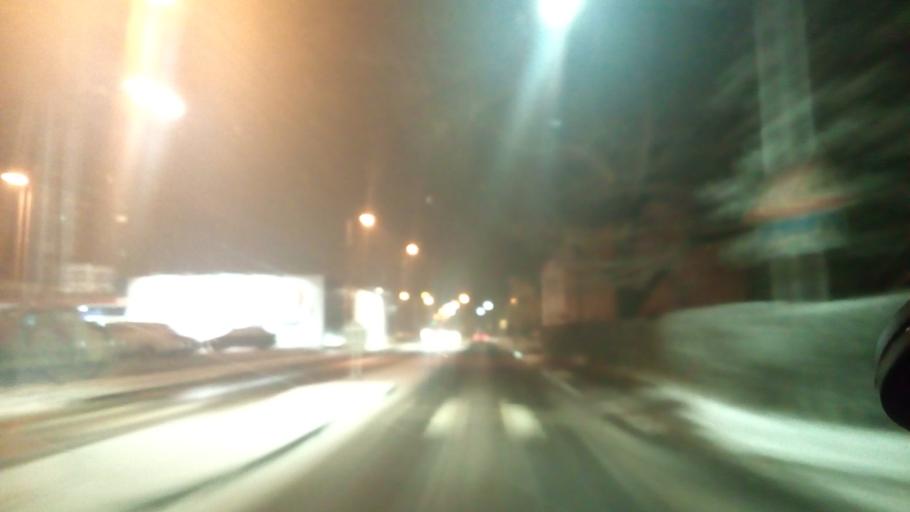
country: CZ
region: Moravskoslezsky
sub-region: Okres Frydek-Mistek
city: Stare Mesto
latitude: 49.6777
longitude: 18.3604
